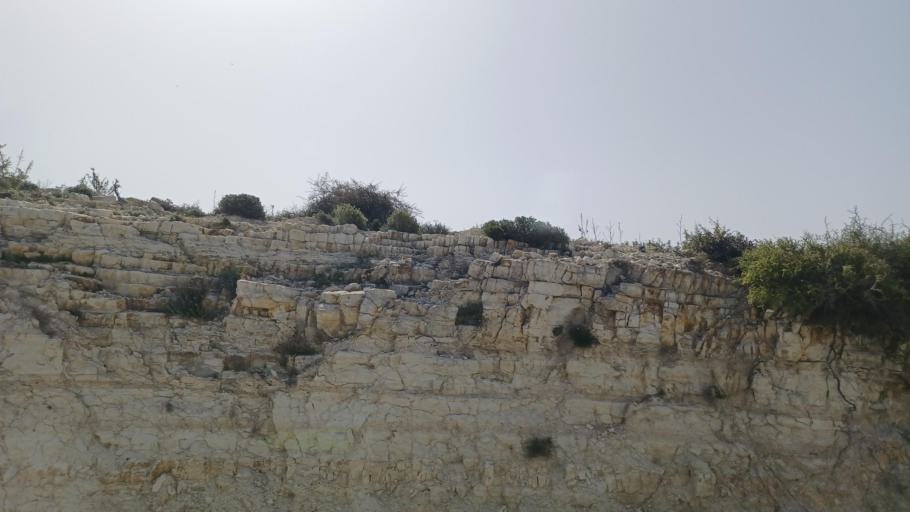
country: CY
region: Limassol
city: Pissouri
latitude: 34.7029
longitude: 32.7058
